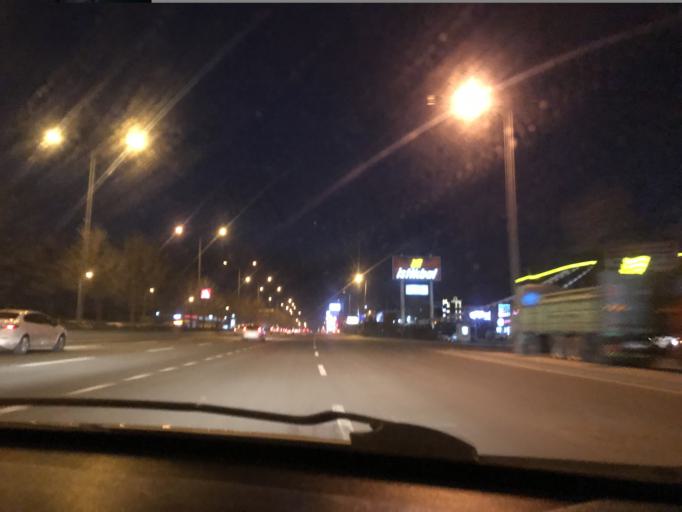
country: TR
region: Ankara
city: Batikent
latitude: 39.9453
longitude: 32.7351
